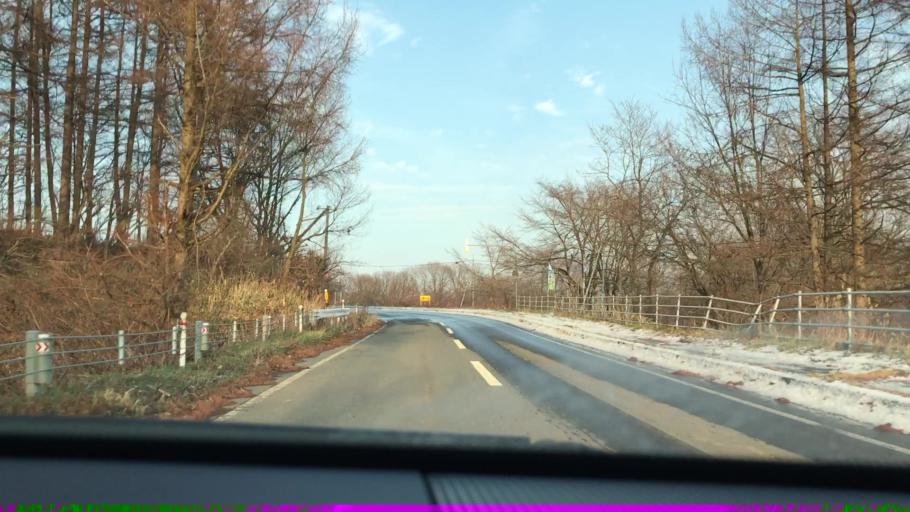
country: JP
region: Hokkaido
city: Shizunai-furukawacho
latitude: 42.4256
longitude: 142.4030
